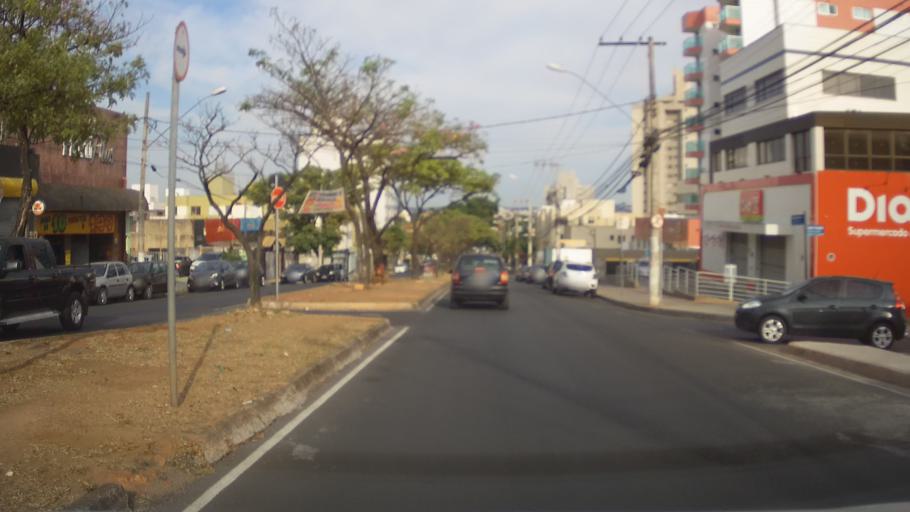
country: BR
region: Minas Gerais
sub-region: Belo Horizonte
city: Belo Horizonte
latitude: -19.8923
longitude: -43.9962
